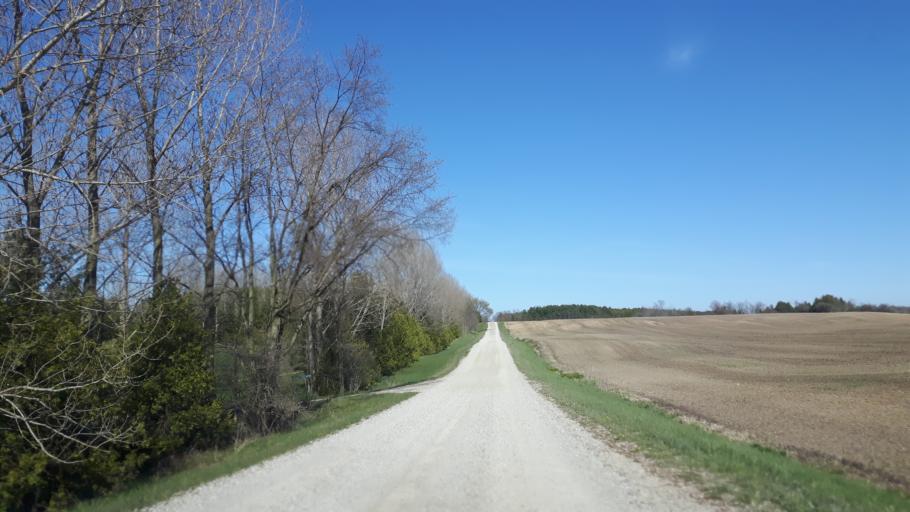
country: CA
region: Ontario
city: Goderich
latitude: 43.6614
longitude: -81.6730
